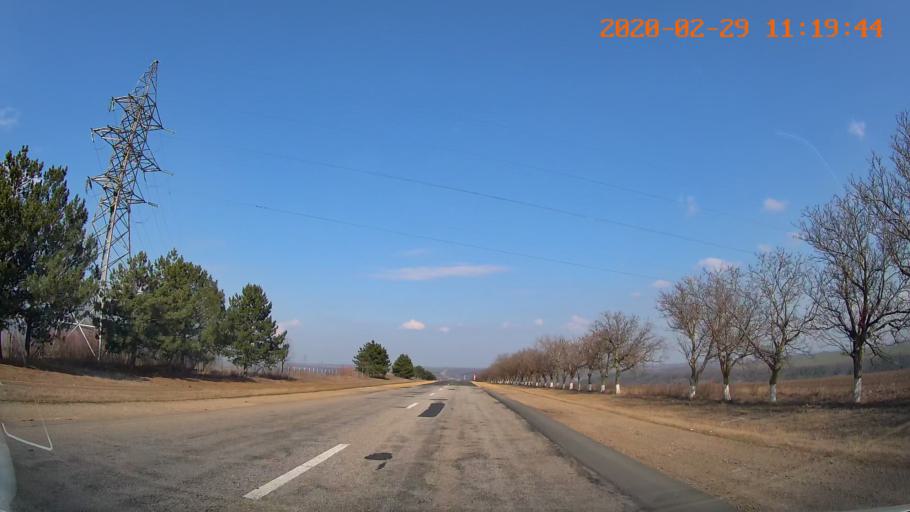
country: MD
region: Telenesti
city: Cocieri
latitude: 47.3545
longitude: 29.1736
